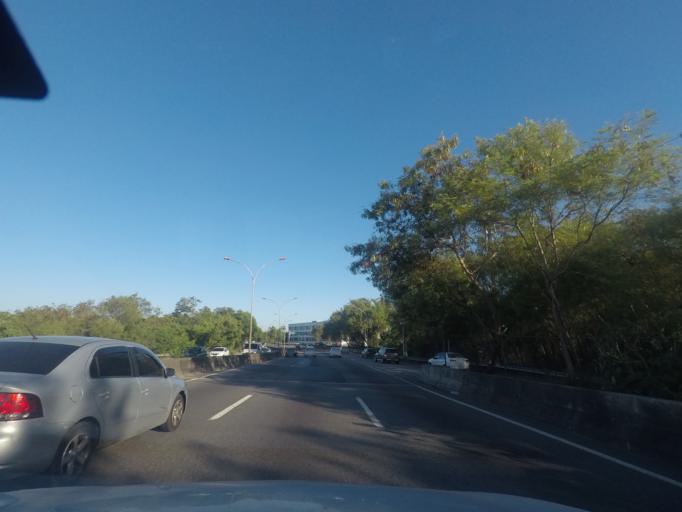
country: BR
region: Rio de Janeiro
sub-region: Duque De Caxias
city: Duque de Caxias
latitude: -22.8312
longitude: -43.2468
